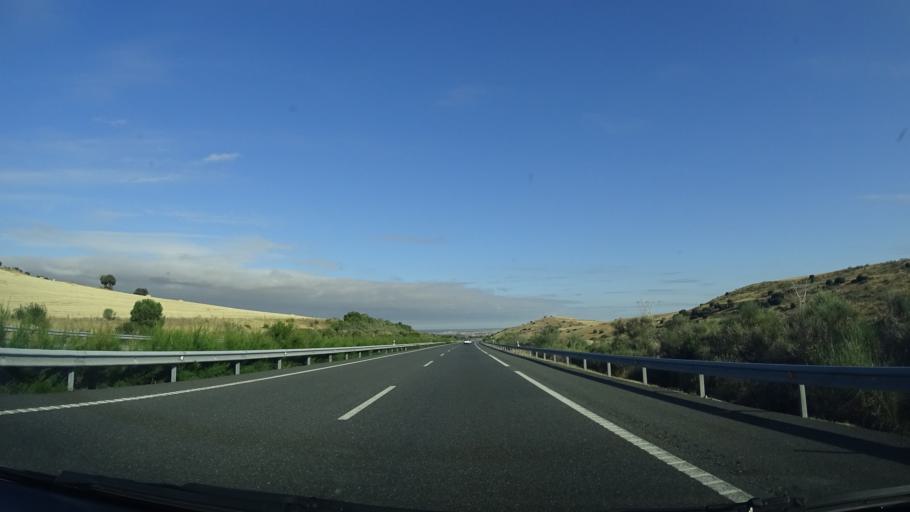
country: ES
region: Castille and Leon
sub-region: Provincia de Segovia
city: Labajos
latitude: 40.8322
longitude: -4.5260
